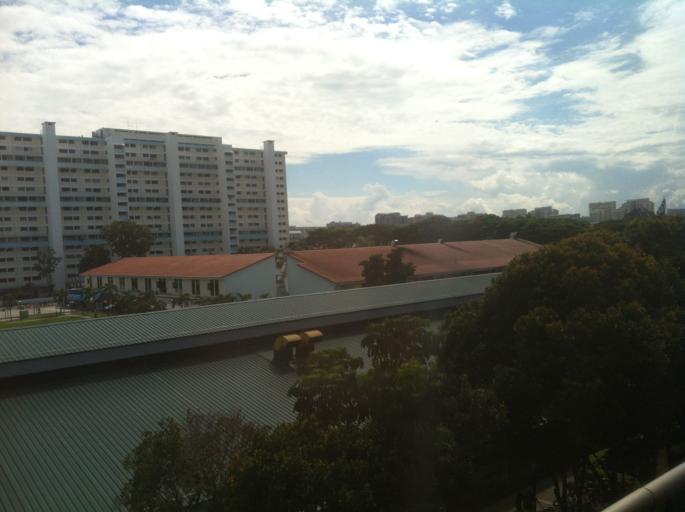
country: SG
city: Singapore
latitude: 1.3200
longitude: 103.9039
